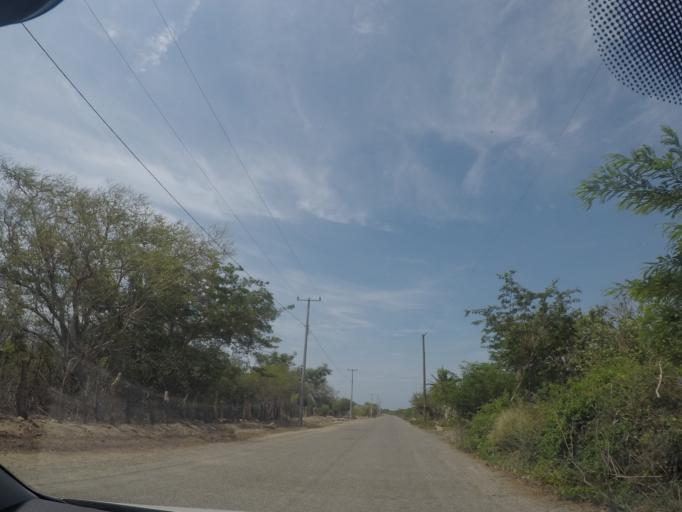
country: MX
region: Oaxaca
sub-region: Salina Cruz
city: Salina Cruz
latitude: 16.1989
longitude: -95.1197
